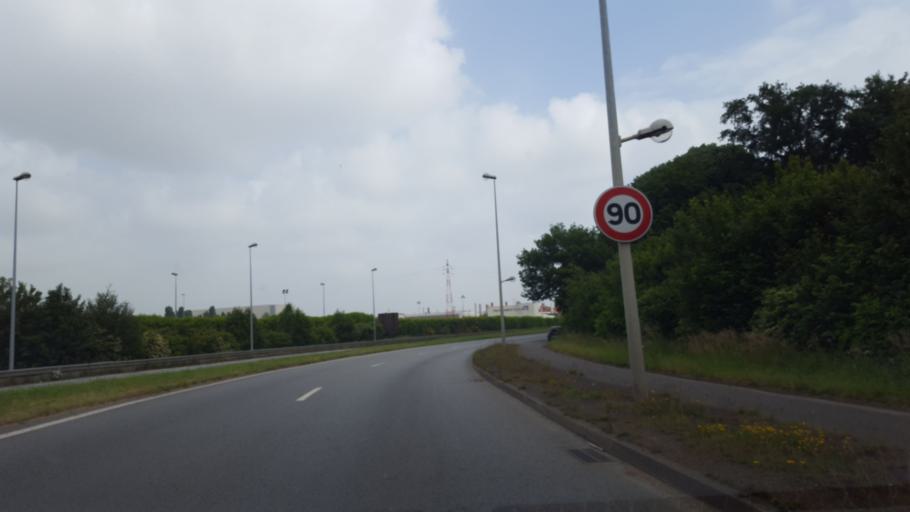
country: FR
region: Brittany
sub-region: Departement d'Ille-et-Vilaine
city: Chartres-de-Bretagne
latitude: 48.0505
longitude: -1.7067
